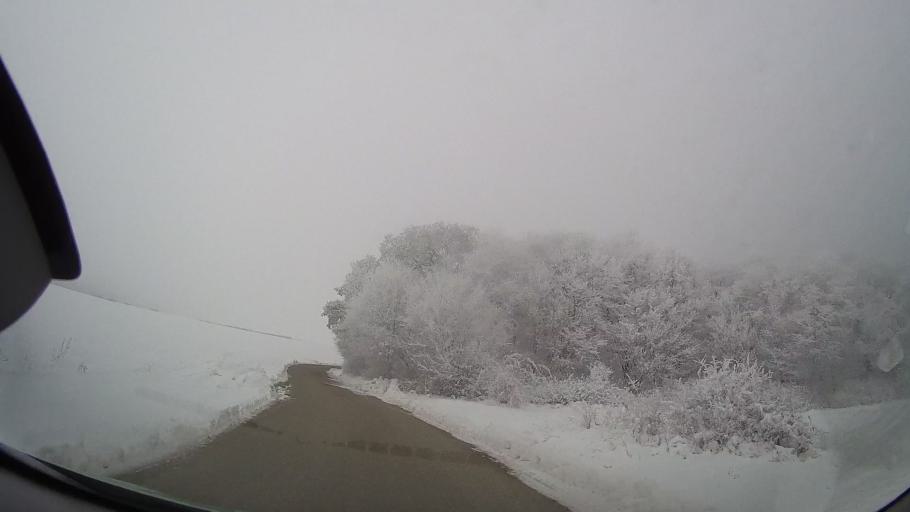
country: RO
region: Iasi
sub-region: Comuna Dagata
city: Dagata
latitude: 46.9090
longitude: 27.1868
